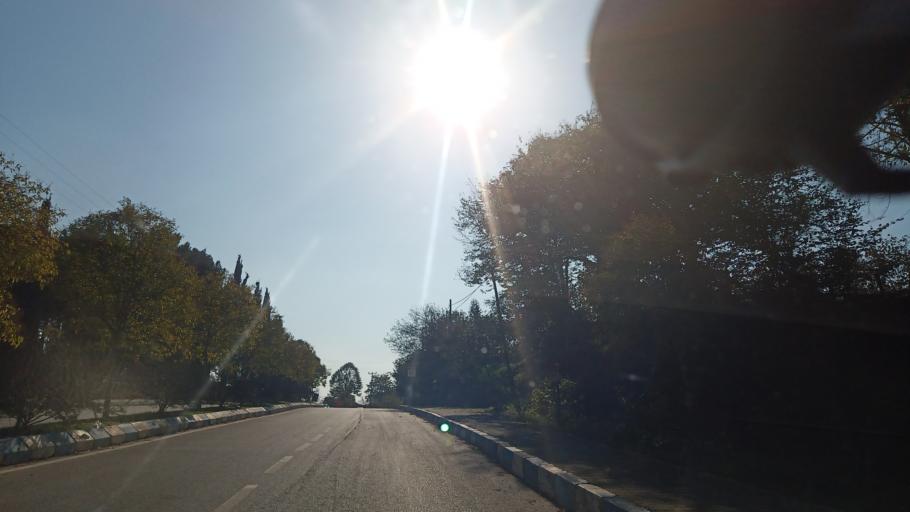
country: TR
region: Sakarya
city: Karasu
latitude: 41.0669
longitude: 30.8030
